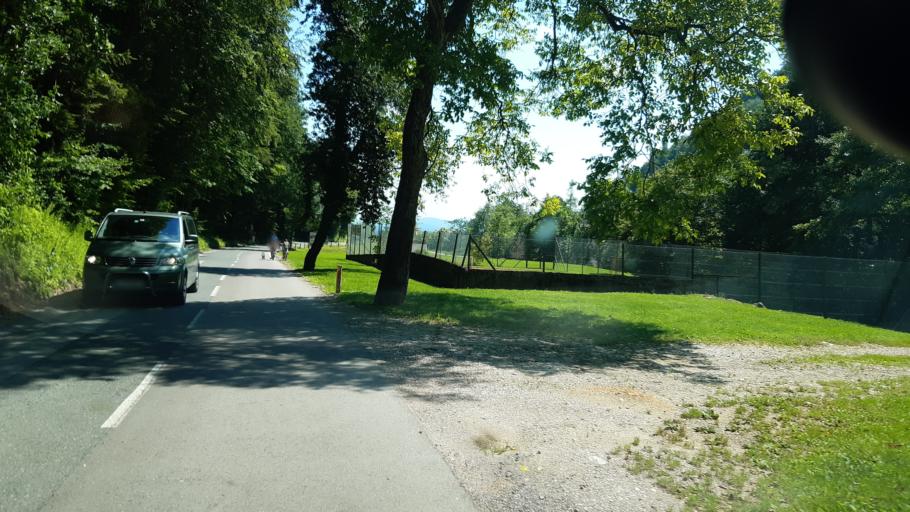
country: SI
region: Cerklje na Gorenjskem
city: Cerklje na Gorenjskem
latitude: 46.2690
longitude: 14.4926
